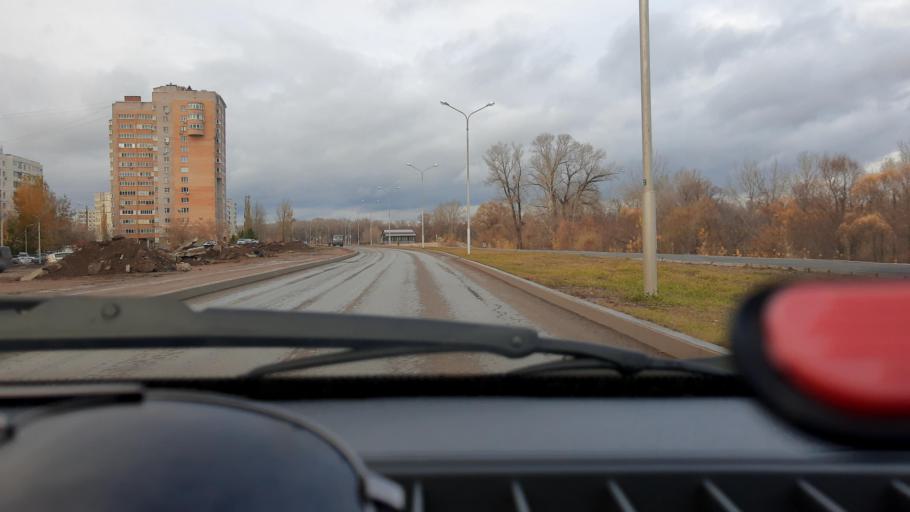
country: RU
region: Bashkortostan
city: Ufa
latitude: 54.7705
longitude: 56.0847
